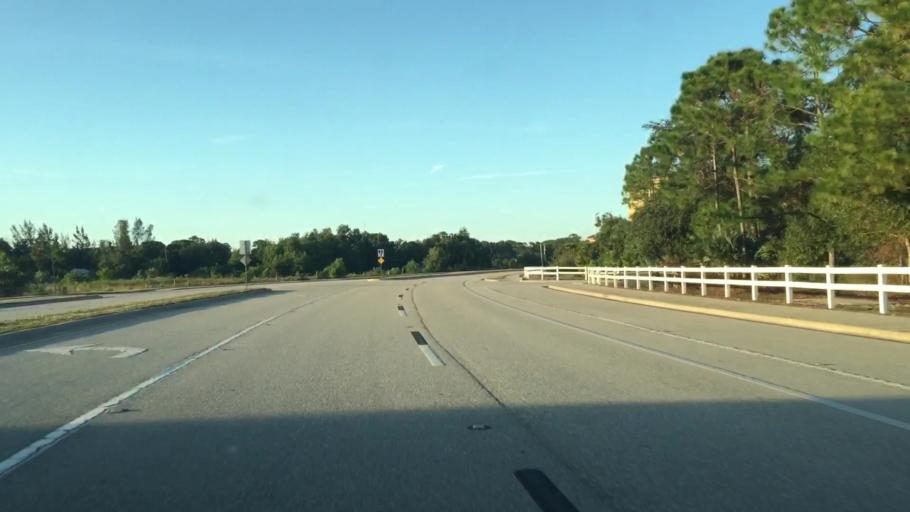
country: US
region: Florida
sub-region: Lee County
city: Estero
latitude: 26.4265
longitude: -81.8043
